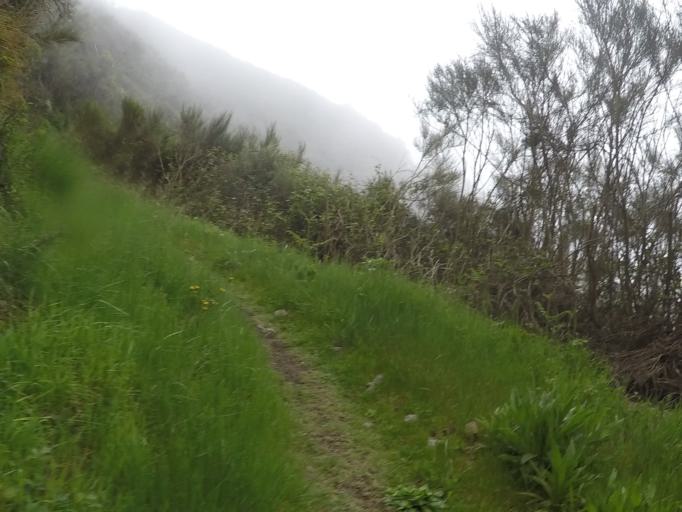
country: PT
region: Madeira
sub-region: Camara de Lobos
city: Curral das Freiras
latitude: 32.7326
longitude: -16.9866
